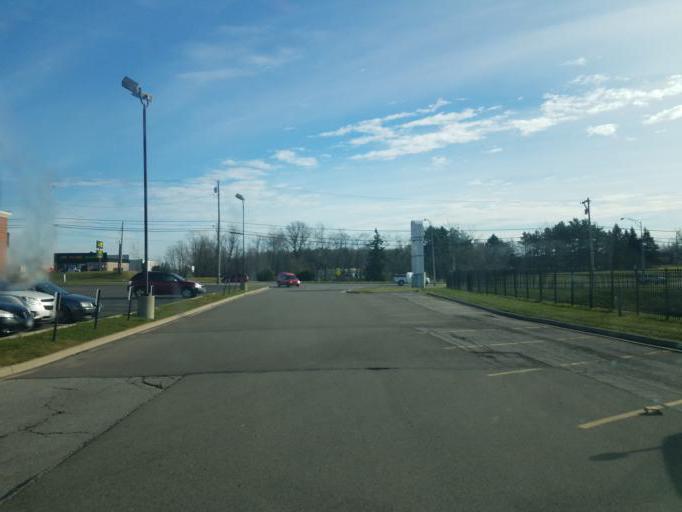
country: US
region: Ohio
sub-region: Richland County
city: Ontario
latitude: 40.7617
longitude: -82.5917
